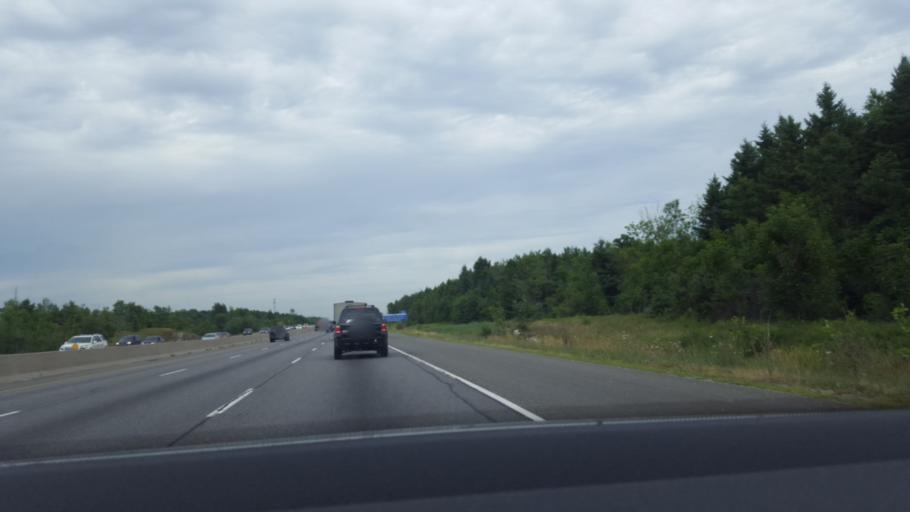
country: CA
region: Ontario
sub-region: Halton
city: Milton
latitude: 43.4754
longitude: -80.0283
